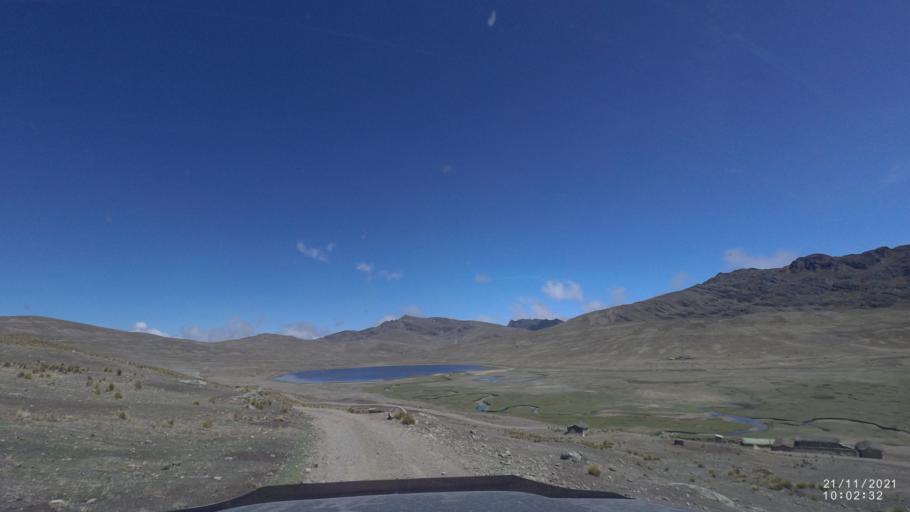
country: BO
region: Cochabamba
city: Cochabamba
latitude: -17.0293
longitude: -66.2745
